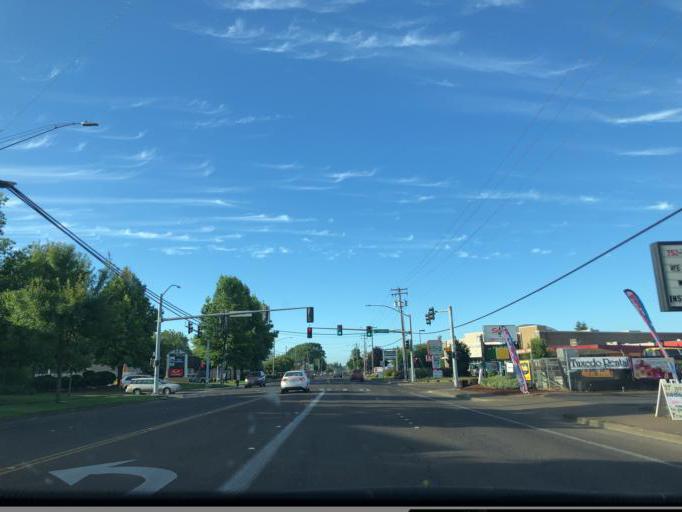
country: US
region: Oregon
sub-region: Benton County
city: Corvallis
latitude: 44.5825
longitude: -123.2583
